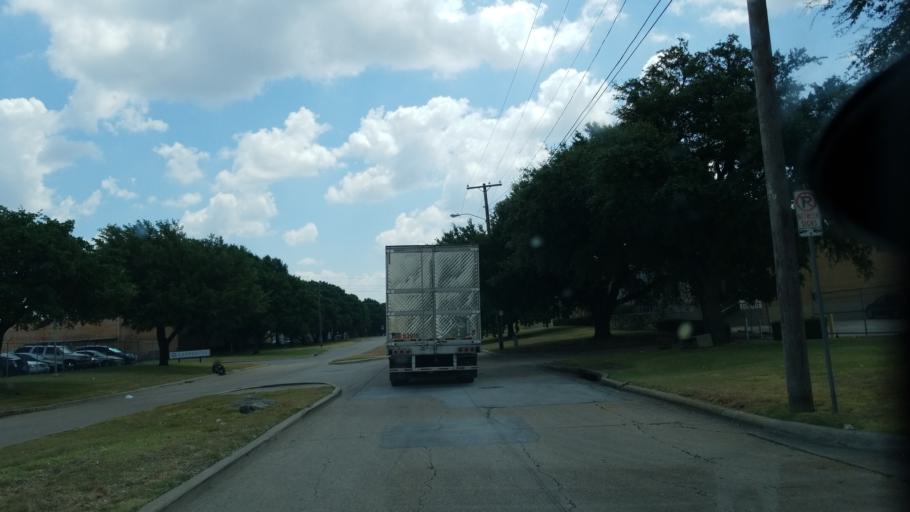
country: US
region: Texas
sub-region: Dallas County
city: Duncanville
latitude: 32.6872
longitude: -96.8939
